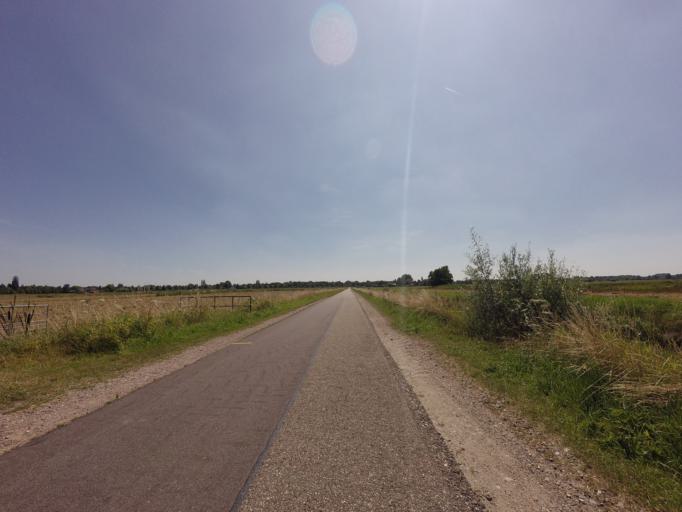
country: NL
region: Utrecht
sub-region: Stichtse Vecht
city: Maarssen
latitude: 52.1571
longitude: 5.0701
